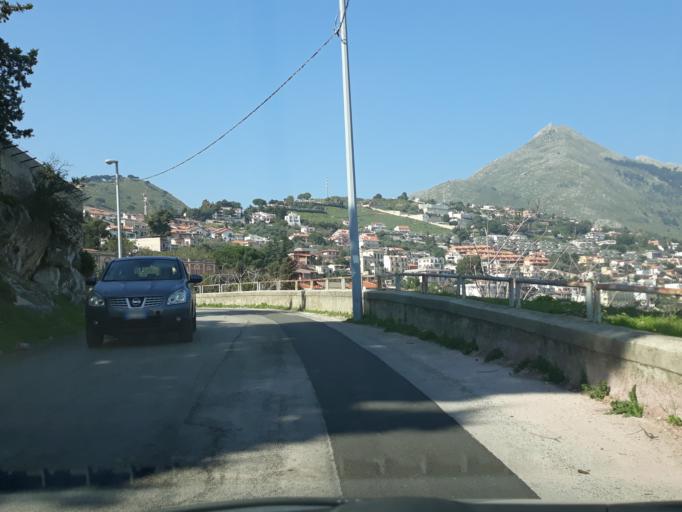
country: IT
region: Sicily
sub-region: Palermo
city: Piano dei Geli
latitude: 38.1101
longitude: 13.3059
